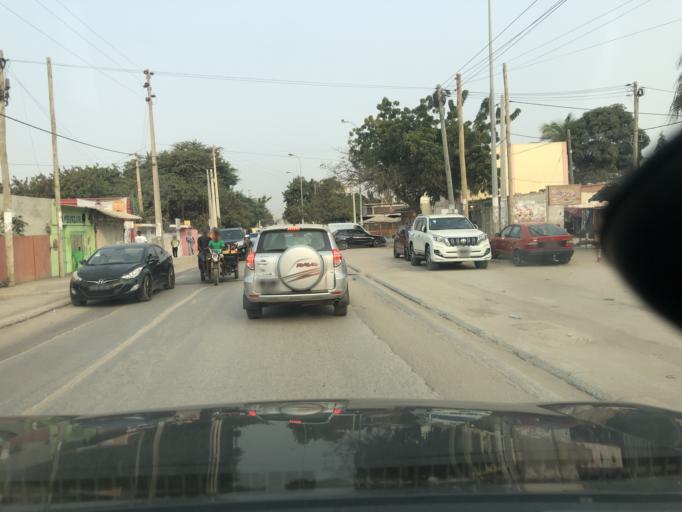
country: AO
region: Luanda
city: Luanda
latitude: -8.8810
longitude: 13.1974
